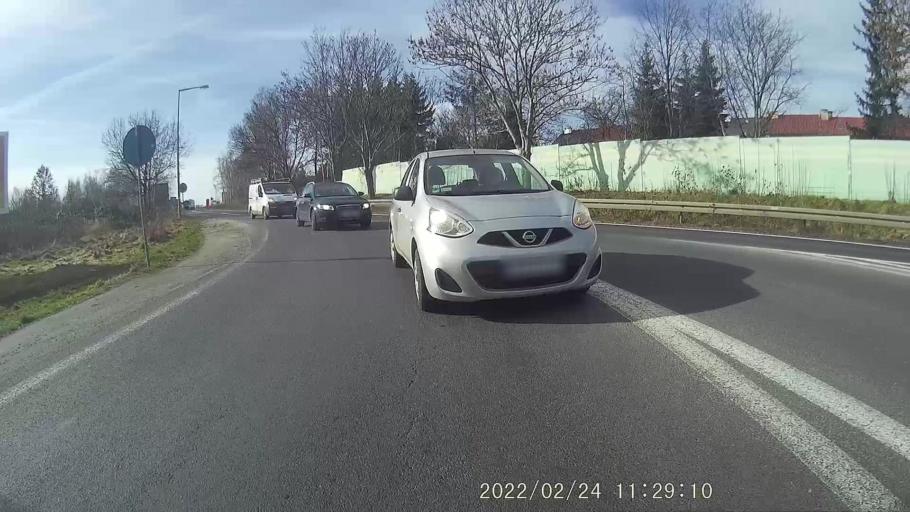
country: PL
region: Lower Silesian Voivodeship
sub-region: Powiat polkowicki
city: Przemkow
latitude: 51.5289
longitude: 15.7009
